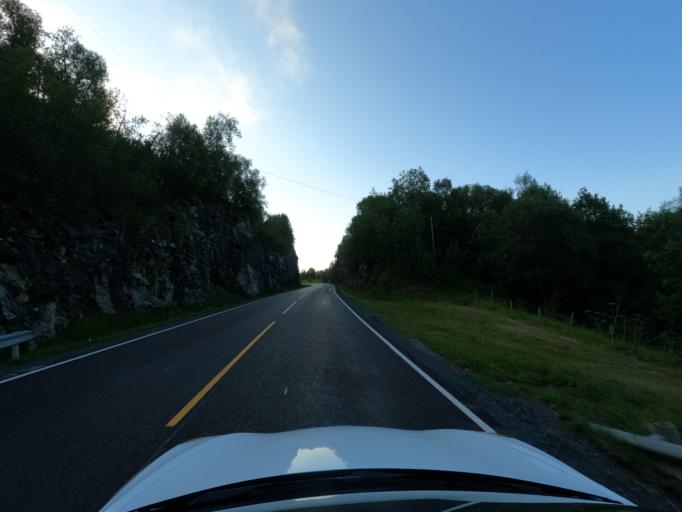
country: NO
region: Troms
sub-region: Skanland
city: Evenskjer
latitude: 68.6722
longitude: 16.5700
